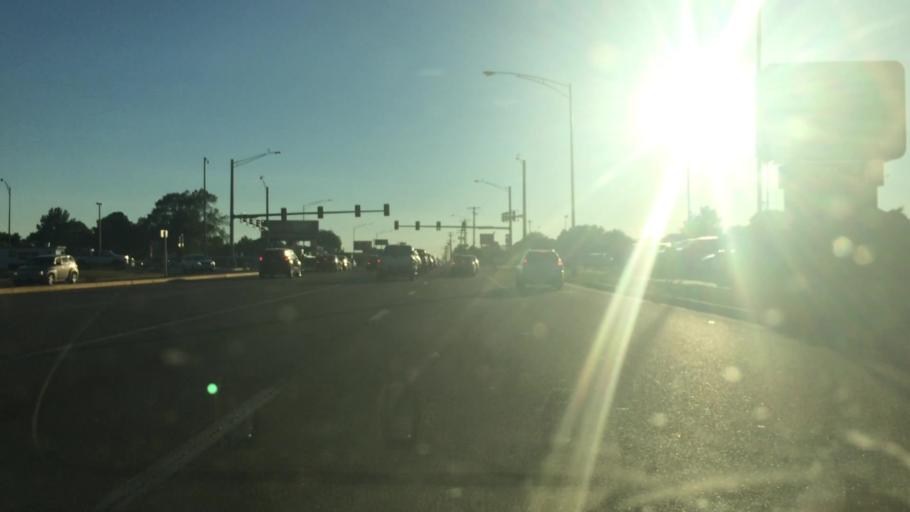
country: US
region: Missouri
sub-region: Greene County
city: Springfield
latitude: 37.1817
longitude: -93.2611
